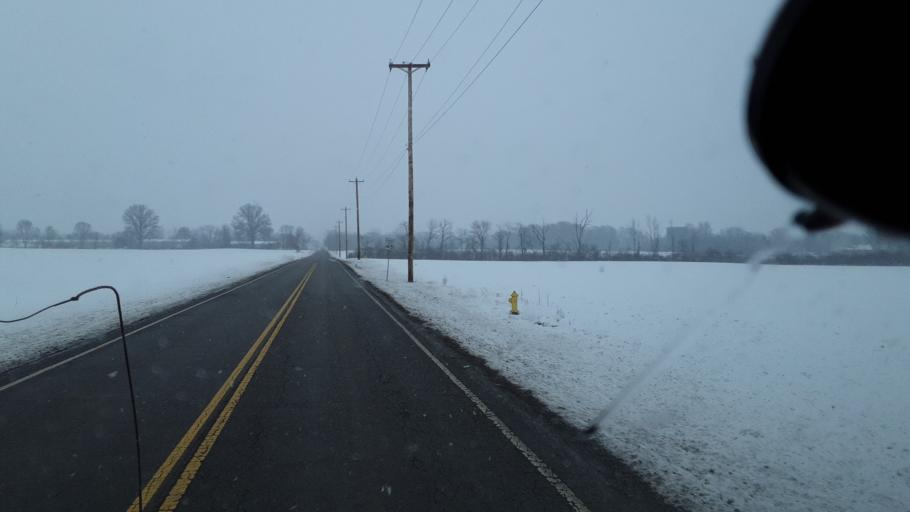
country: US
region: Ohio
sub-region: Licking County
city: Hebron
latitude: 40.0004
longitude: -82.4820
